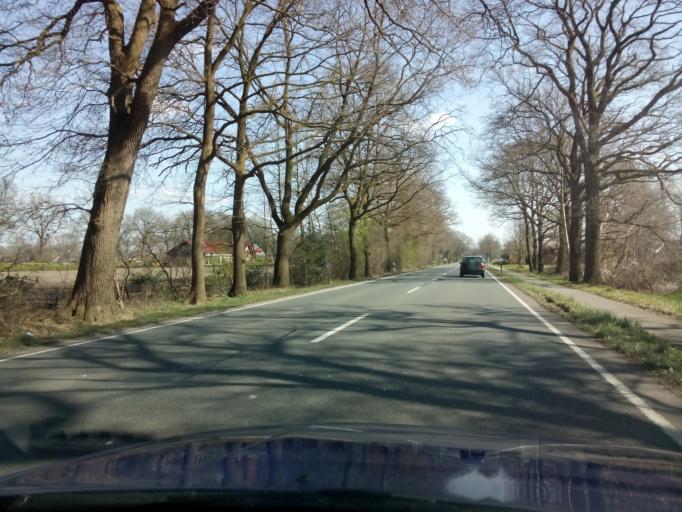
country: DE
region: Lower Saxony
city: Emlichheim
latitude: 52.6093
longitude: 6.8313
